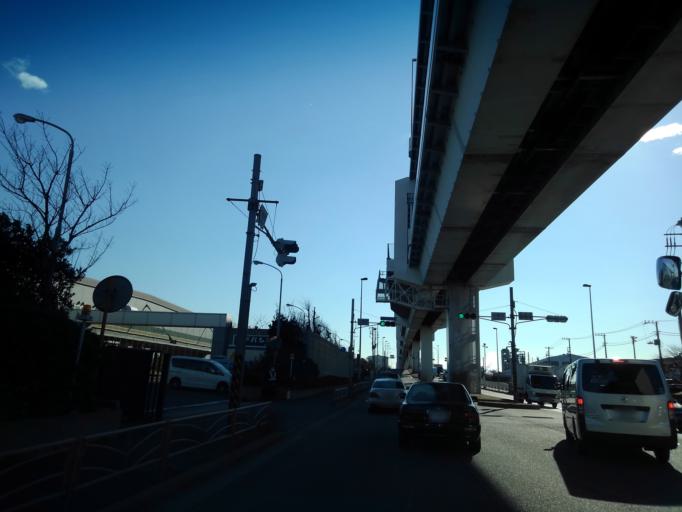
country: JP
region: Kanagawa
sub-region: Kawasaki-shi
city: Kawasaki
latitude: 35.5356
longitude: 139.7624
